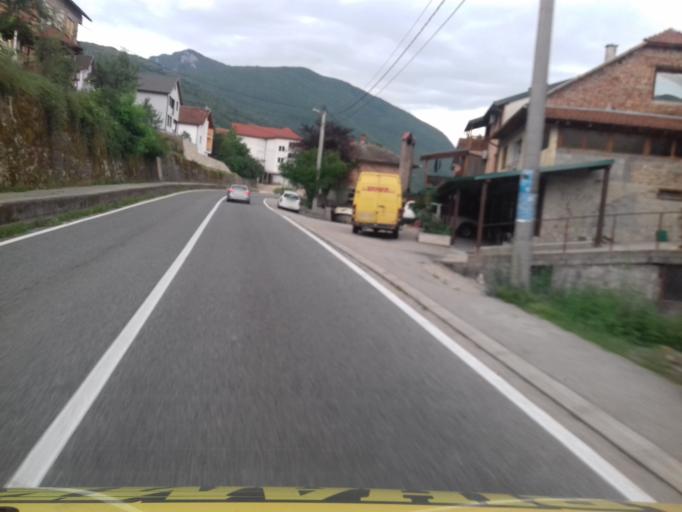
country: BA
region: Federation of Bosnia and Herzegovina
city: Jablanica
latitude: 43.6842
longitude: 17.8272
